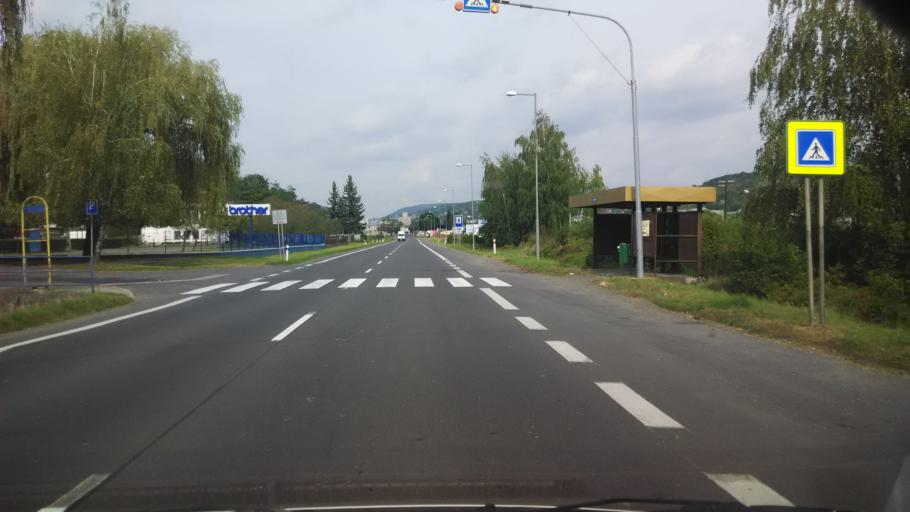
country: SK
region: Banskobystricky
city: Krupina
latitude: 48.3382
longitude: 19.0645
